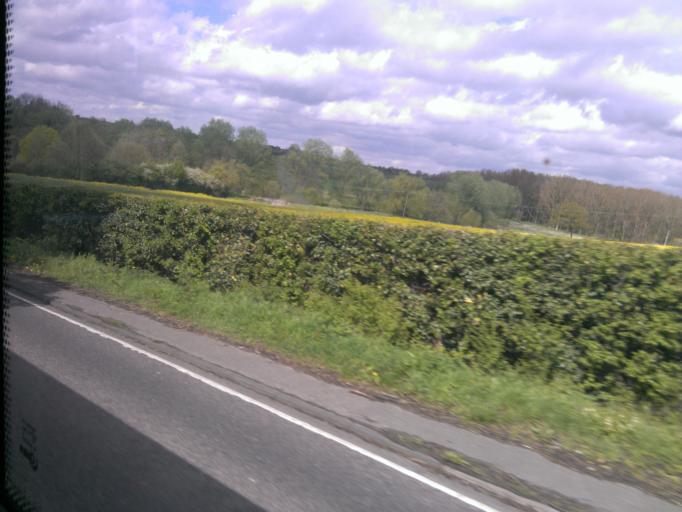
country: GB
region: England
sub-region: Essex
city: Eight Ash Green
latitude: 51.9052
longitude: 0.7926
